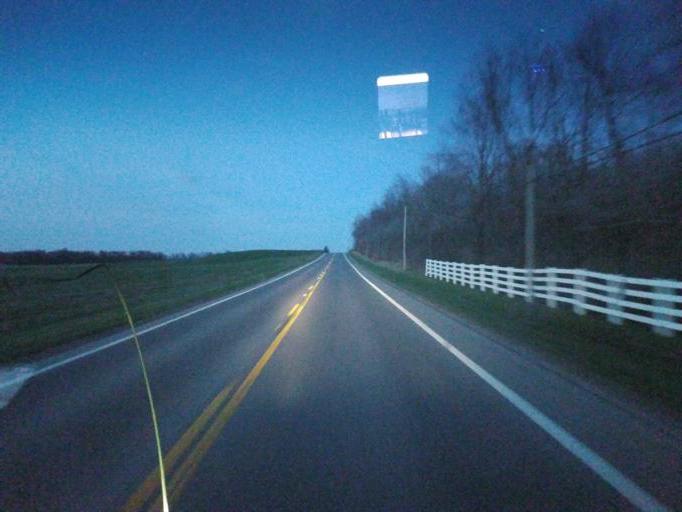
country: US
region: Ohio
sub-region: Logan County
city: De Graff
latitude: 40.3561
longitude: -83.8888
